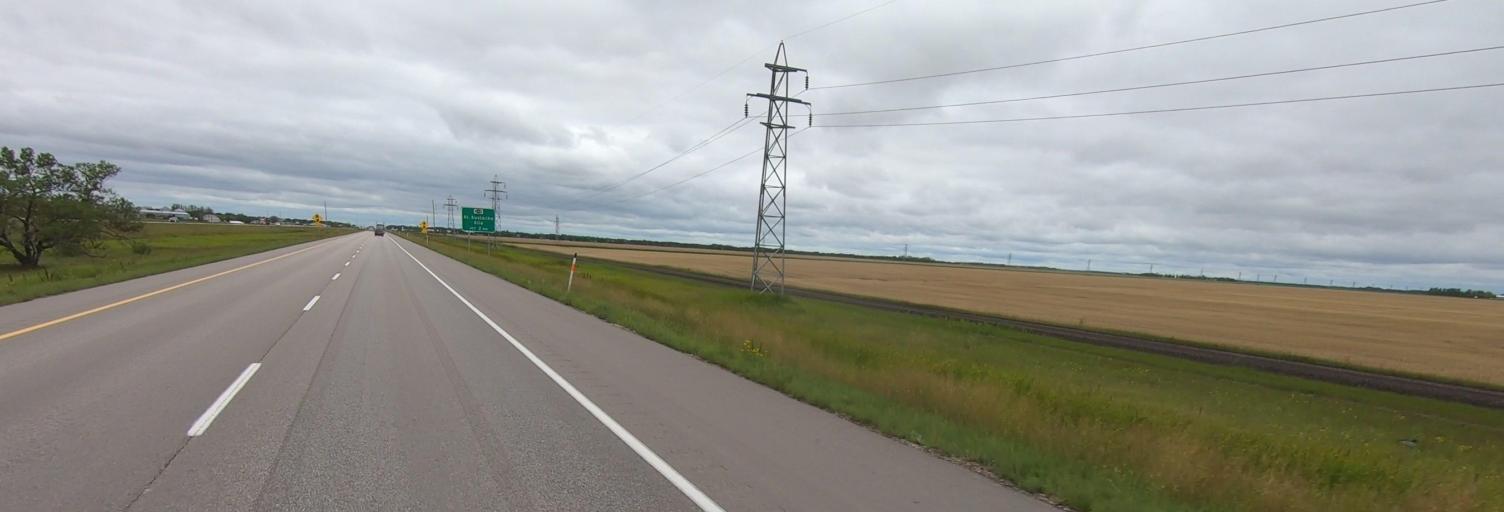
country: CA
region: Manitoba
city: Headingley
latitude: 49.9003
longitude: -97.7295
